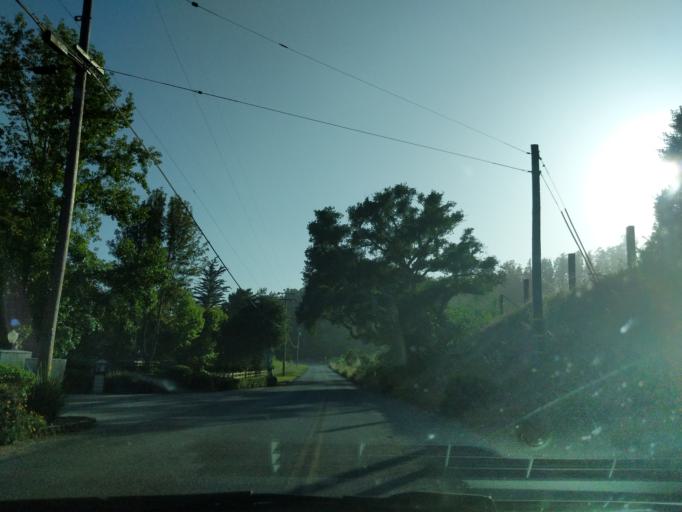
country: US
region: California
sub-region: Monterey County
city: Las Lomas
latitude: 36.8848
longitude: -121.7279
